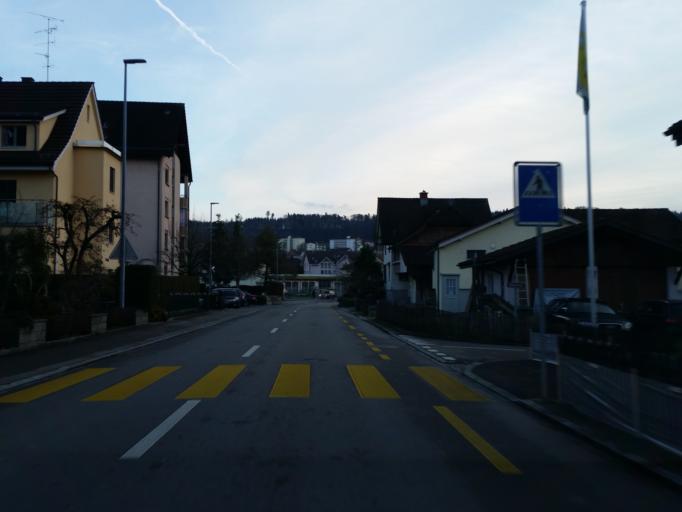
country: CH
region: Saint Gallen
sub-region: Wahlkreis Wil
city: Niederburen
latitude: 47.5005
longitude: 9.2385
